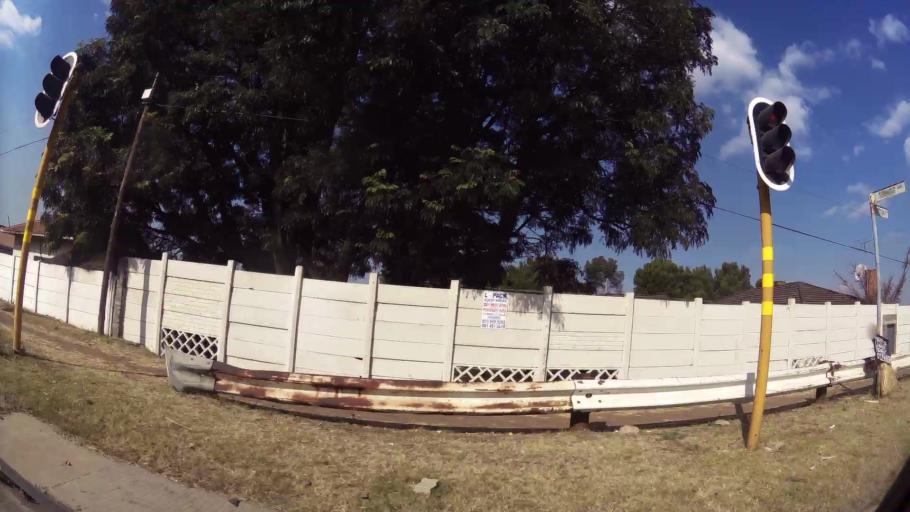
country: ZA
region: Gauteng
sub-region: Ekurhuleni Metropolitan Municipality
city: Germiston
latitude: -26.1808
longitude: 28.1786
